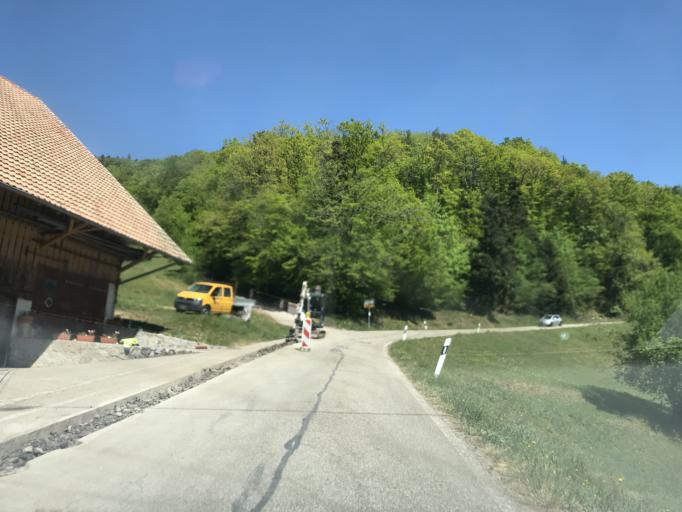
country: DE
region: Baden-Wuerttemberg
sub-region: Freiburg Region
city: Hausen
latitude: 47.6802
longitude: 7.8690
